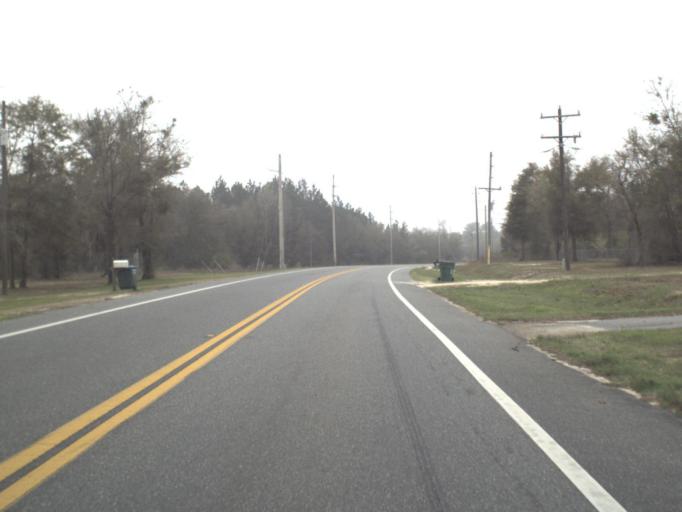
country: US
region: Florida
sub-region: Liberty County
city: Bristol
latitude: 30.3989
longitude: -84.7902
